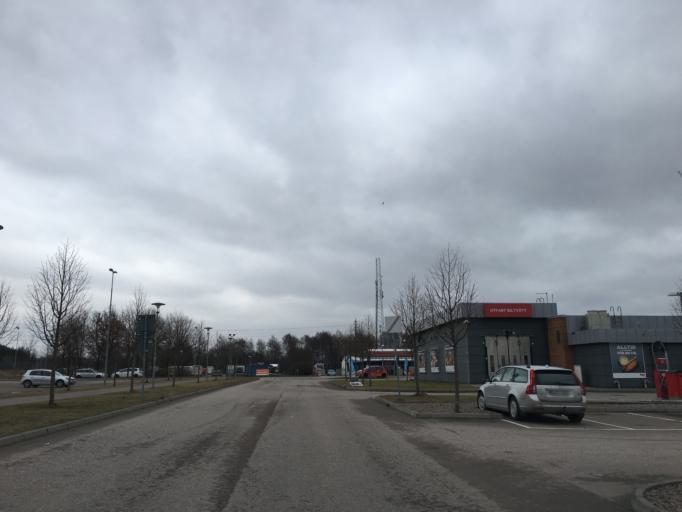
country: SE
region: Halland
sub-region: Halmstads Kommun
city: Halmstad
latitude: 56.6741
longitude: 12.8910
